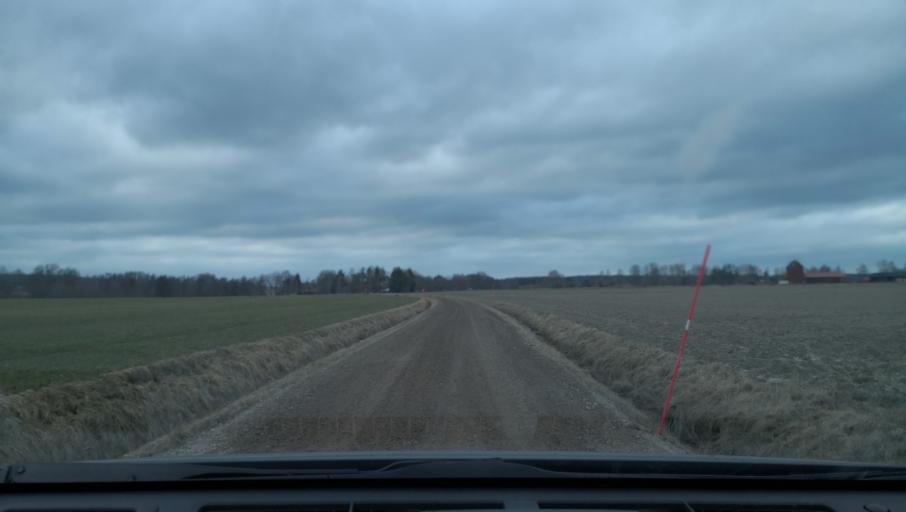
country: SE
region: Vaestmanland
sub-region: Kopings Kommun
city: Kolsva
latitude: 59.5360
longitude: 15.8946
